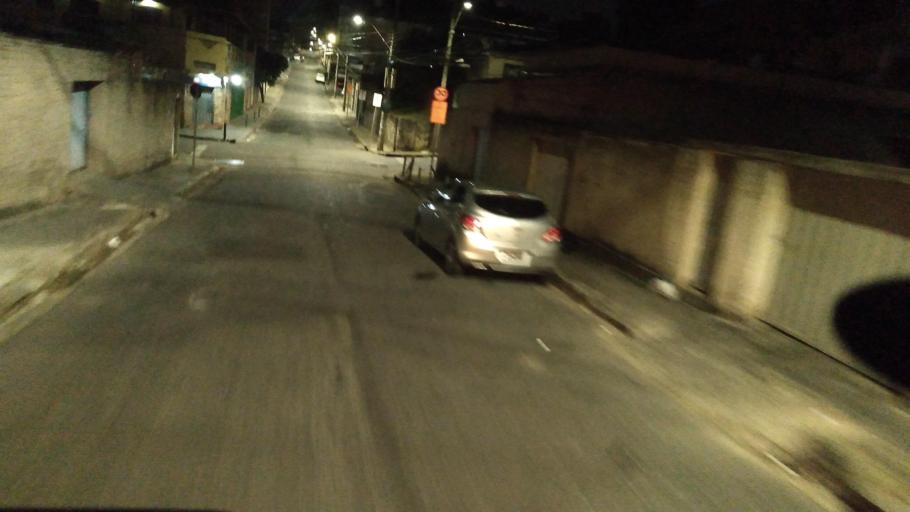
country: BR
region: Minas Gerais
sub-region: Belo Horizonte
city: Belo Horizonte
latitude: -19.8894
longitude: -43.9631
